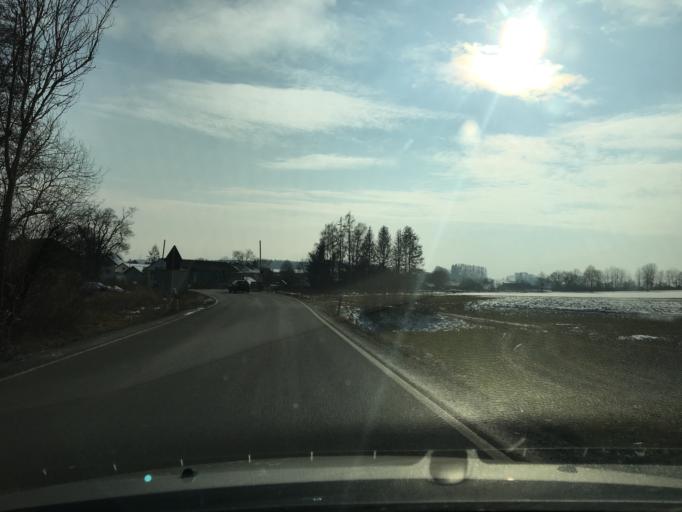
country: DE
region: Bavaria
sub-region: Upper Bavaria
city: Neumarkt-Sankt Veit
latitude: 48.3847
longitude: 12.5496
